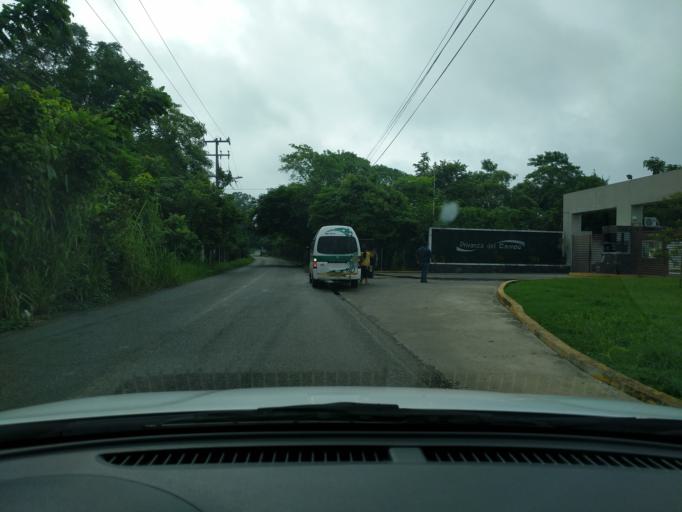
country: MX
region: Tabasco
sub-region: Centro
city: La Lima
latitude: 17.9482
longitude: -92.9633
